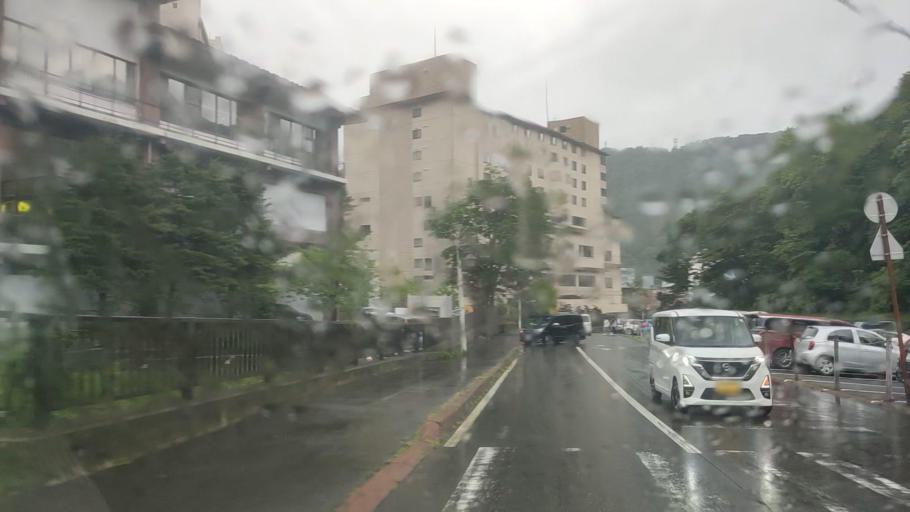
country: JP
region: Hokkaido
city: Shiraoi
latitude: 42.4962
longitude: 141.1453
